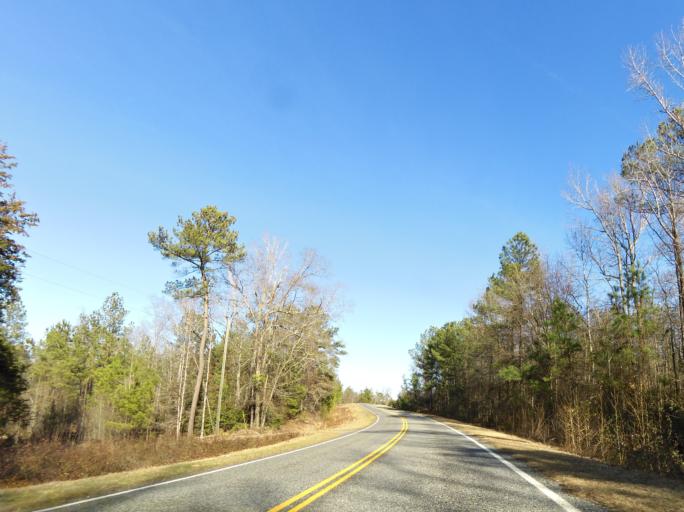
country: US
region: Georgia
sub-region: Crawford County
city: Knoxville
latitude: 32.7260
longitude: -83.9797
